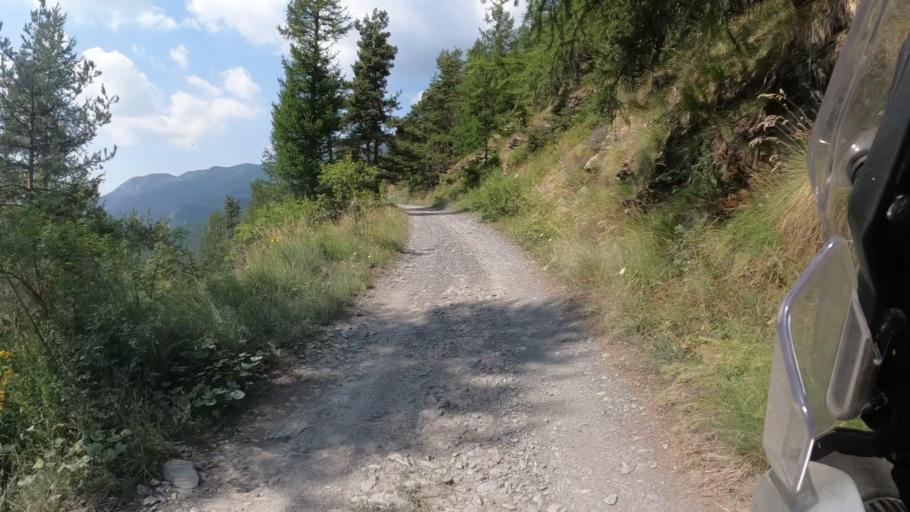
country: IT
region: Piedmont
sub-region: Provincia di Cuneo
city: Briga Alta
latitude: 44.0388
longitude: 7.6896
